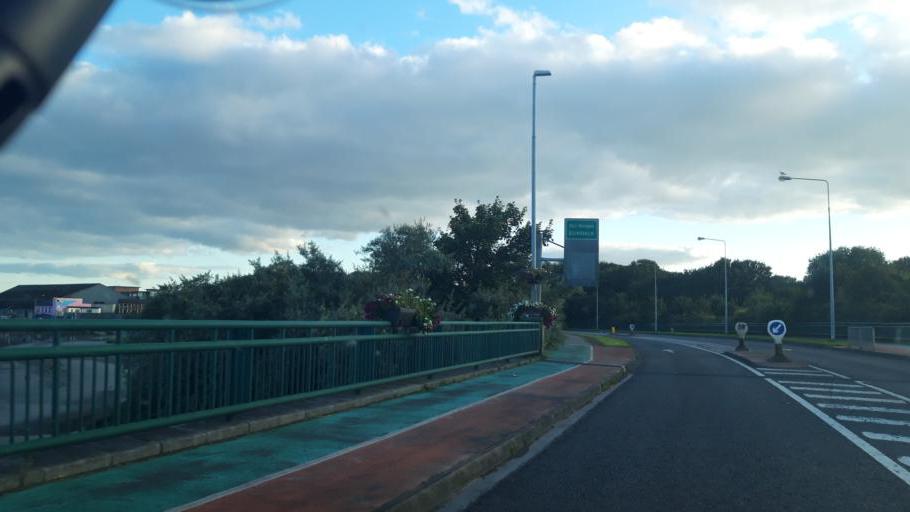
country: IE
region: Leinster
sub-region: Lu
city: Dundalk
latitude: 54.0117
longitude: -6.3918
